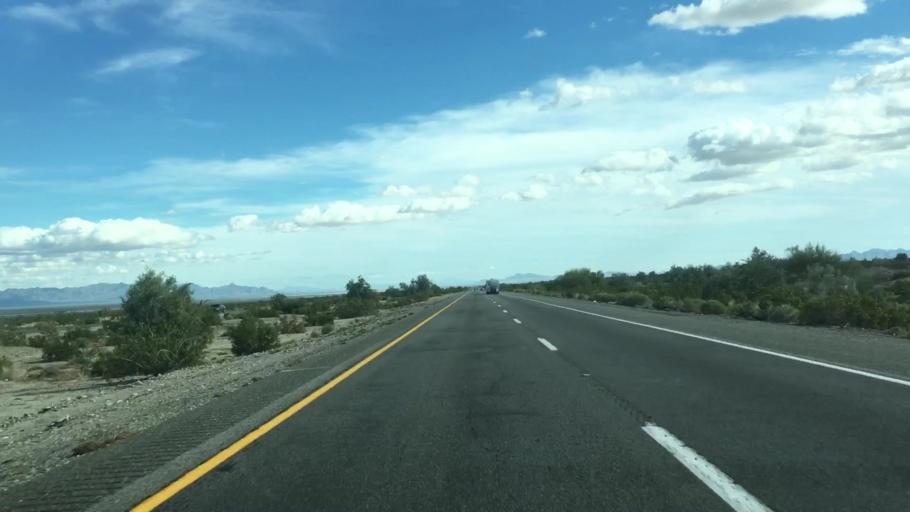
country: US
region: California
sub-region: Riverside County
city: Mesa Verde
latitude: 33.6750
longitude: -115.2190
